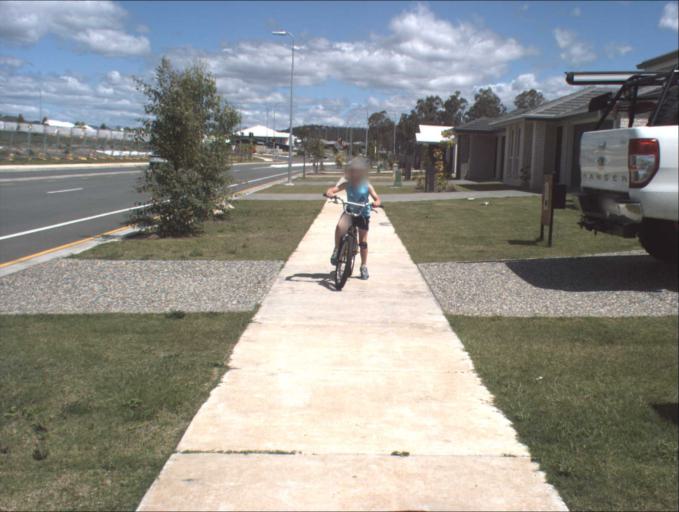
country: AU
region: Queensland
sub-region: Logan
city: Chambers Flat
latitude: -27.8035
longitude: 153.1124
